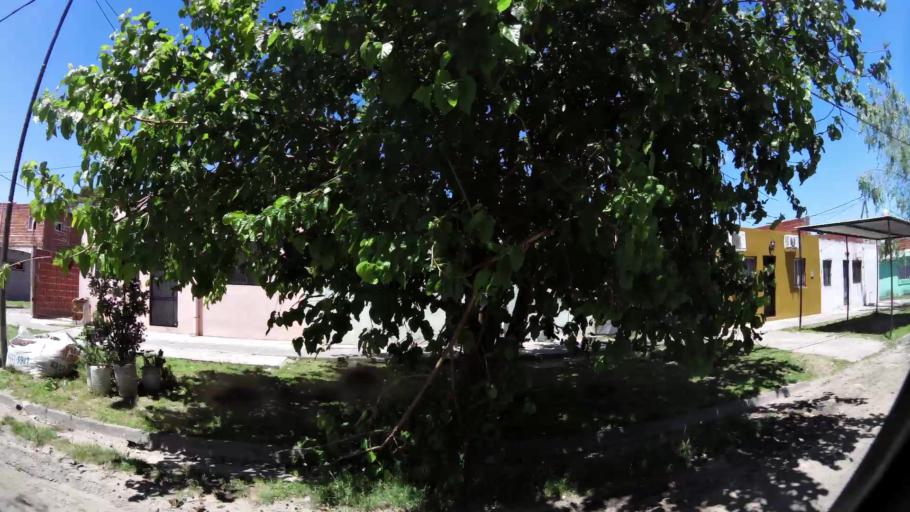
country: AR
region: Buenos Aires
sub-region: Partido de Quilmes
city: Quilmes
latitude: -34.7138
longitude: -58.3147
